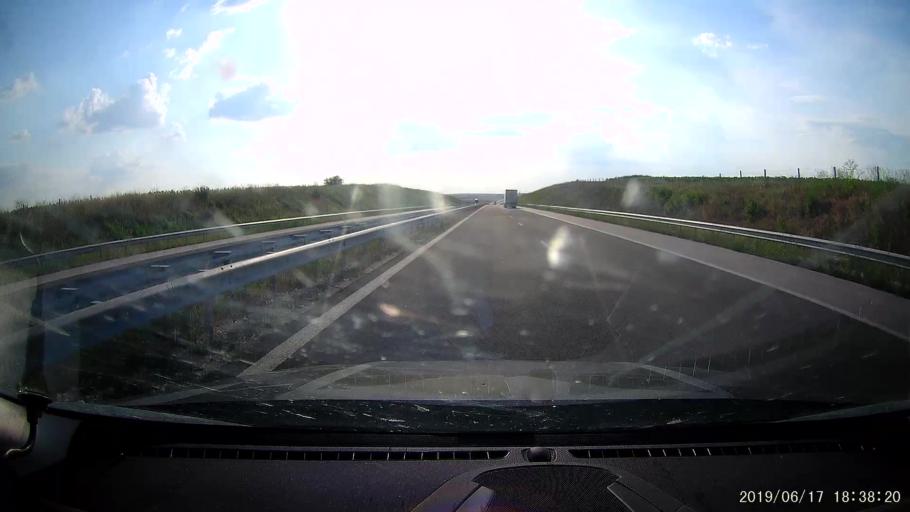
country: BG
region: Stara Zagora
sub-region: Obshtina Chirpan
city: Chirpan
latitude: 42.1363
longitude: 25.3400
